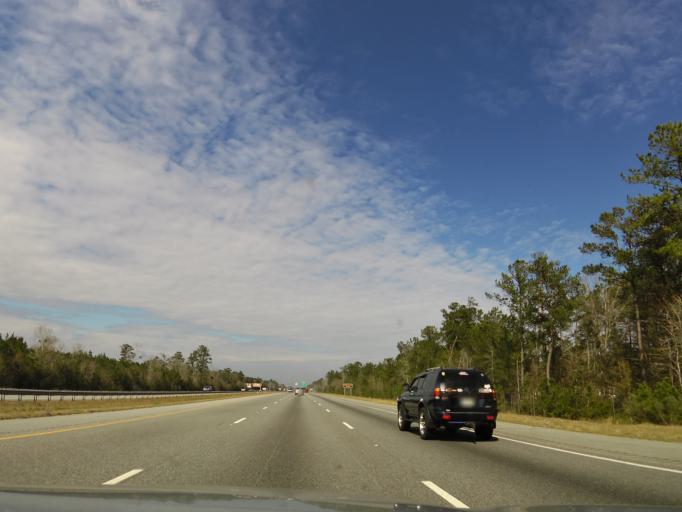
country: US
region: Georgia
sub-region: McIntosh County
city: Darien
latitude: 31.5082
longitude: -81.4460
